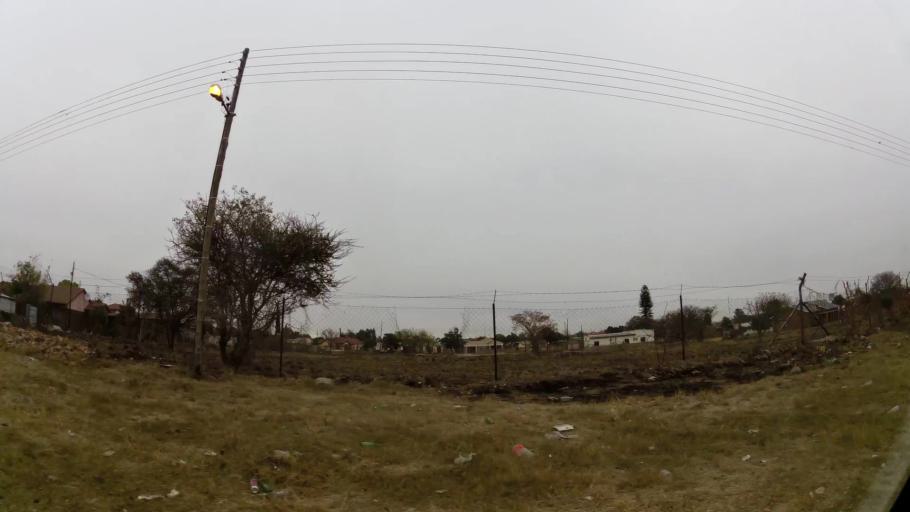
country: ZA
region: Limpopo
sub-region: Capricorn District Municipality
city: Polokwane
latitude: -23.8516
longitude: 29.3951
